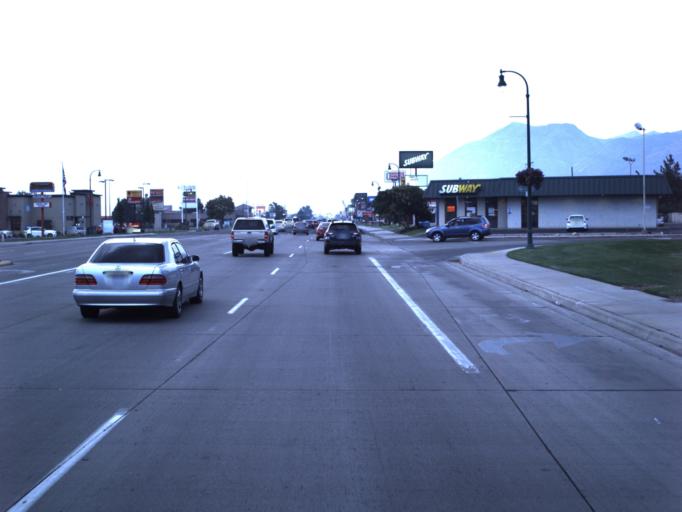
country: US
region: Utah
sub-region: Utah County
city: Orem
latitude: 40.2985
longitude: -111.6955
